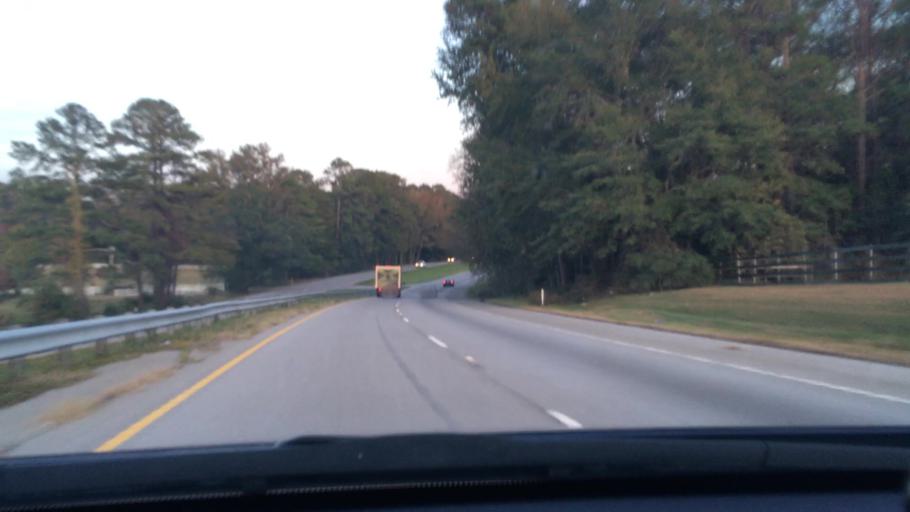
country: US
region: South Carolina
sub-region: Richland County
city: Gadsden
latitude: 33.9457
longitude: -80.7605
